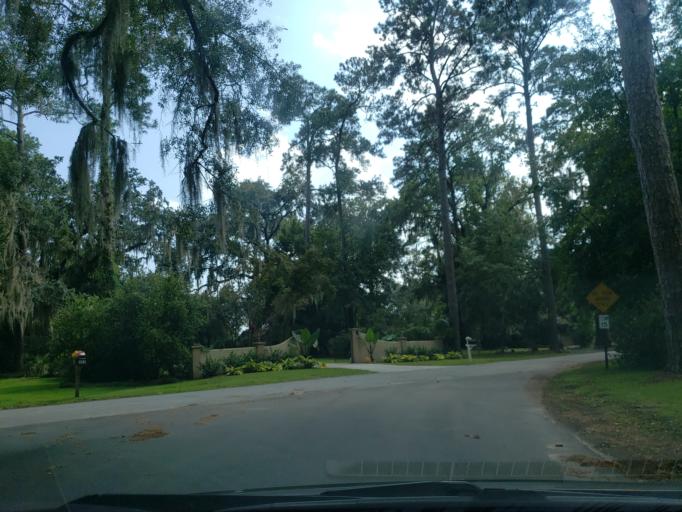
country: US
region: Georgia
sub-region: Chatham County
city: Montgomery
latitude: 31.9287
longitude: -81.0916
